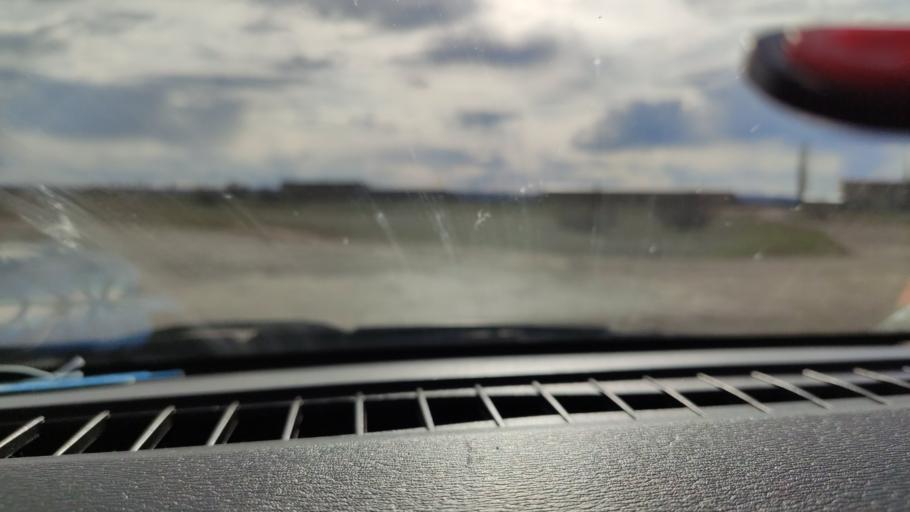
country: RU
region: Saratov
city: Rovnoye
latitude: 50.9355
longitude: 46.0944
